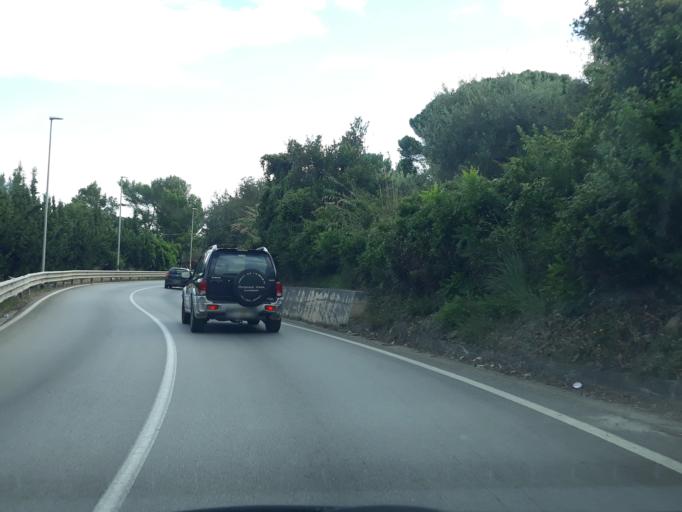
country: IT
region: Sicily
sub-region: Palermo
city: Cefalu
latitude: 38.0284
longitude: 13.9907
